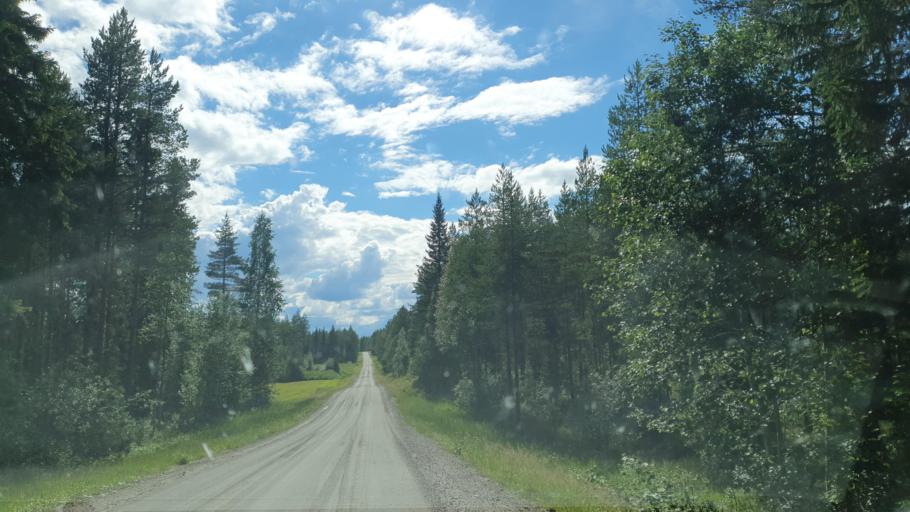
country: FI
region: Kainuu
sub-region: Kehys-Kainuu
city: Kuhmo
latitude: 64.1476
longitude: 29.7180
